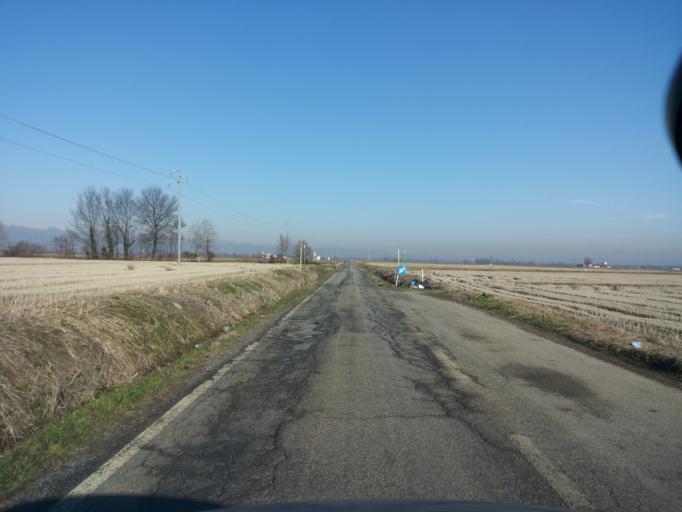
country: IT
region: Piedmont
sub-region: Provincia di Vercelli
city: Formigliana
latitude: 45.4244
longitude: 8.2543
